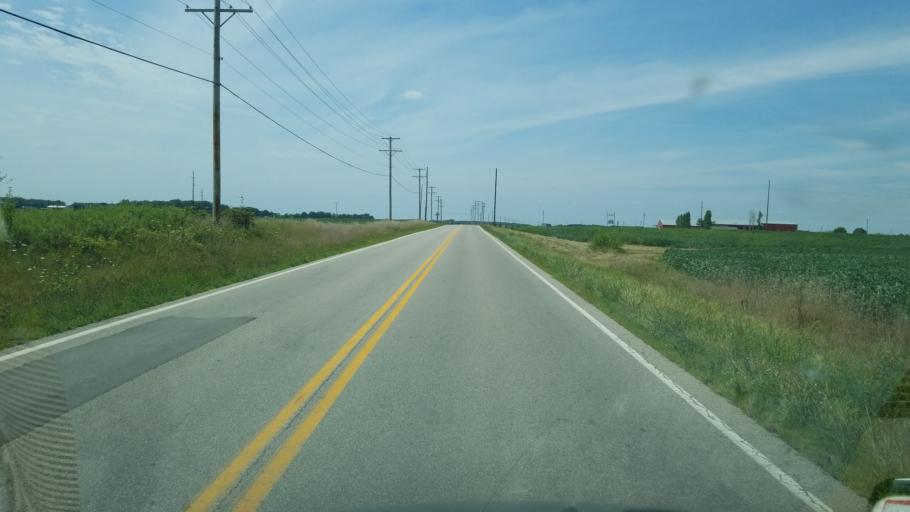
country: US
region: Ohio
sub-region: Union County
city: New California
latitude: 40.2028
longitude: -83.1841
